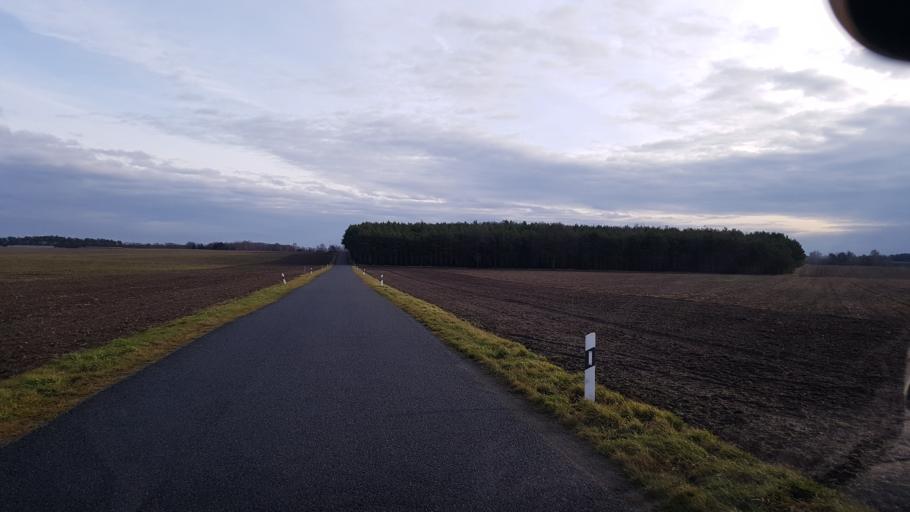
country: DE
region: Brandenburg
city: Bronkow
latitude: 51.6586
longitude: 13.8851
